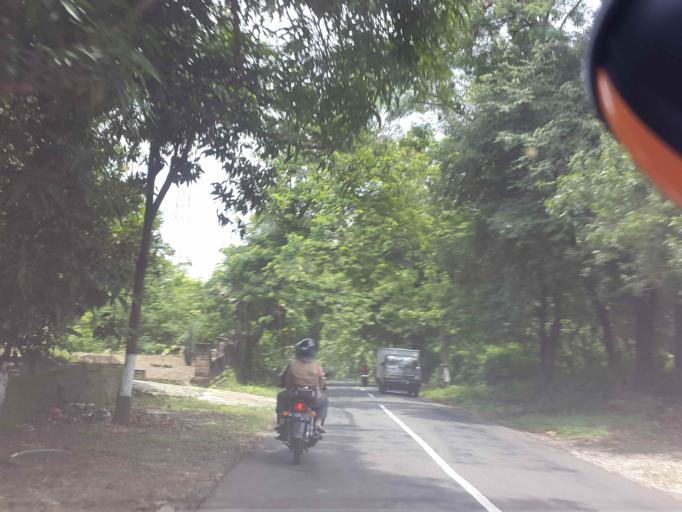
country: ID
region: East Java
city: Ponorogo
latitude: -7.7205
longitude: 111.3568
